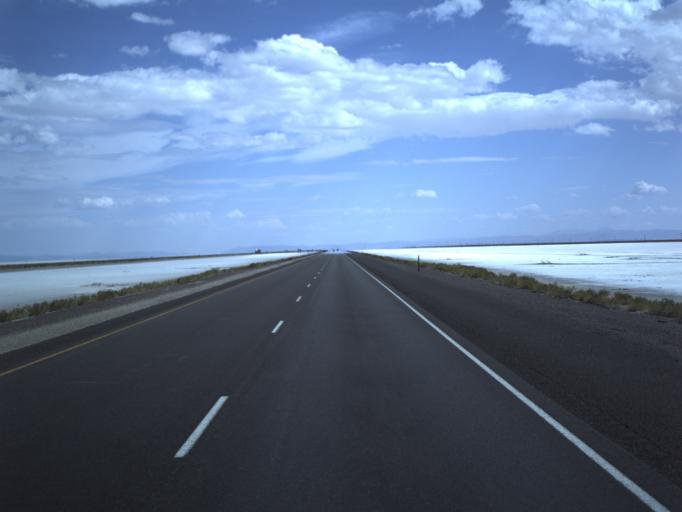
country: US
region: Utah
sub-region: Tooele County
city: Wendover
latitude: 40.7358
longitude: -113.7190
